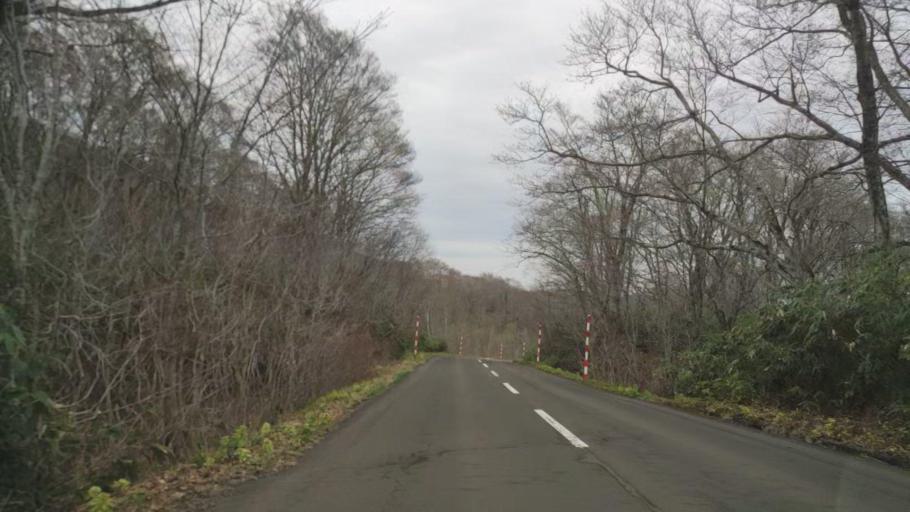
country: JP
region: Akita
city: Hanawa
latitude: 40.4180
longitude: 140.8205
